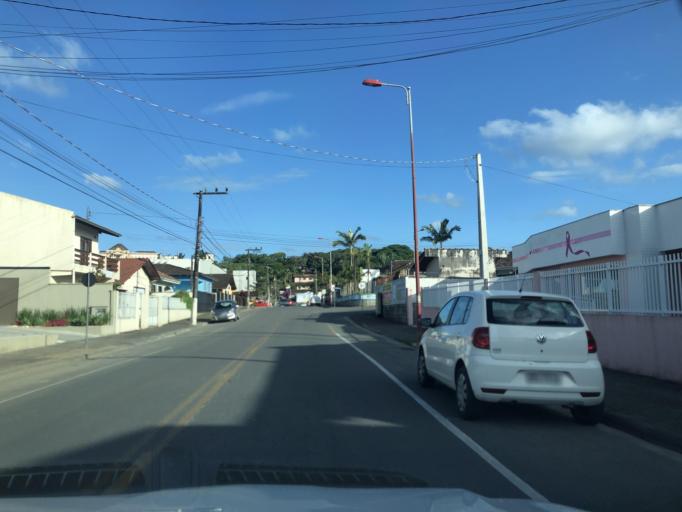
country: BR
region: Santa Catarina
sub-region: Sao Francisco Do Sul
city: Sao Francisco do Sul
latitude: -26.2496
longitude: -48.6381
